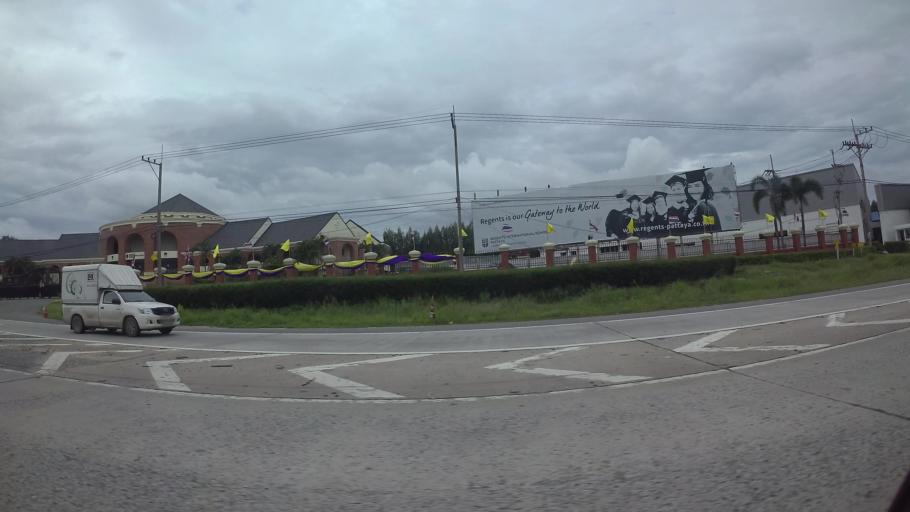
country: TH
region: Chon Buri
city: Bang Lamung
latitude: 12.9701
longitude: 100.9738
